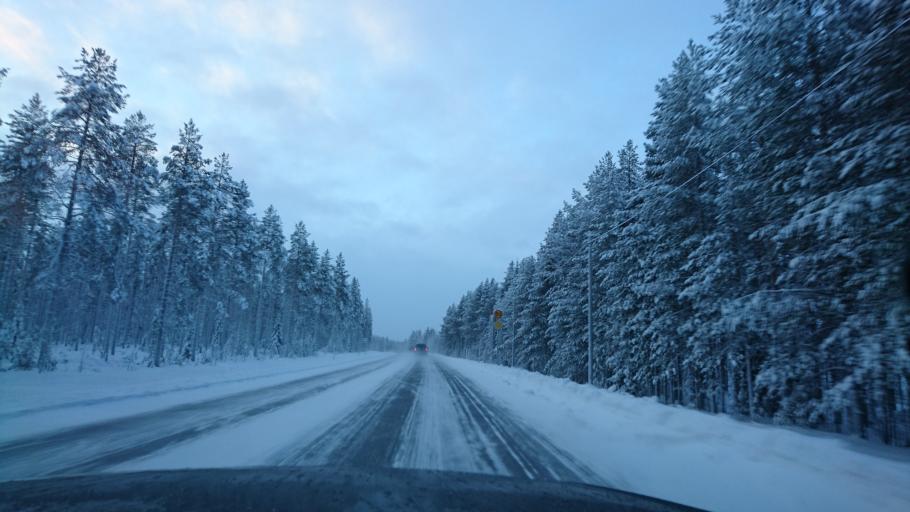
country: FI
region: Kainuu
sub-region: Kehys-Kainuu
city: Puolanka
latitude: 65.4632
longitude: 27.6449
